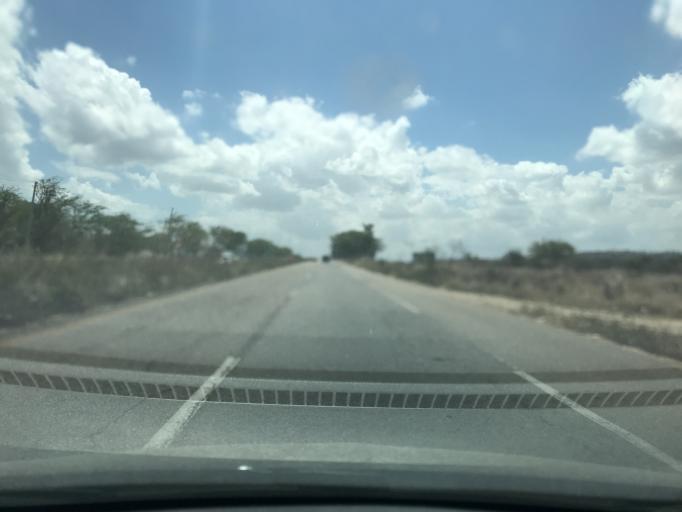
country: BR
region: Pernambuco
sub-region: Bezerros
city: Bezerros
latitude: -8.2974
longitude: -35.8646
